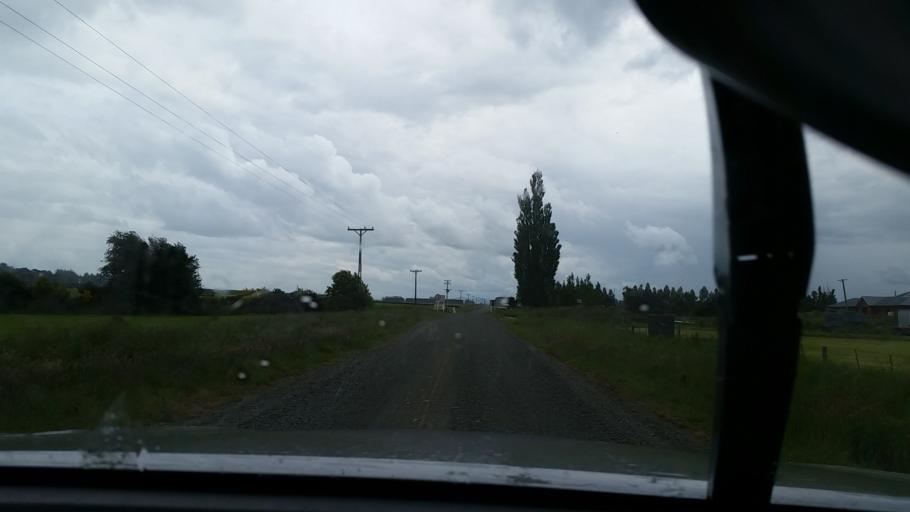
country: NZ
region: Southland
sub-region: Southland District
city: Winton
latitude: -46.0068
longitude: 168.2323
